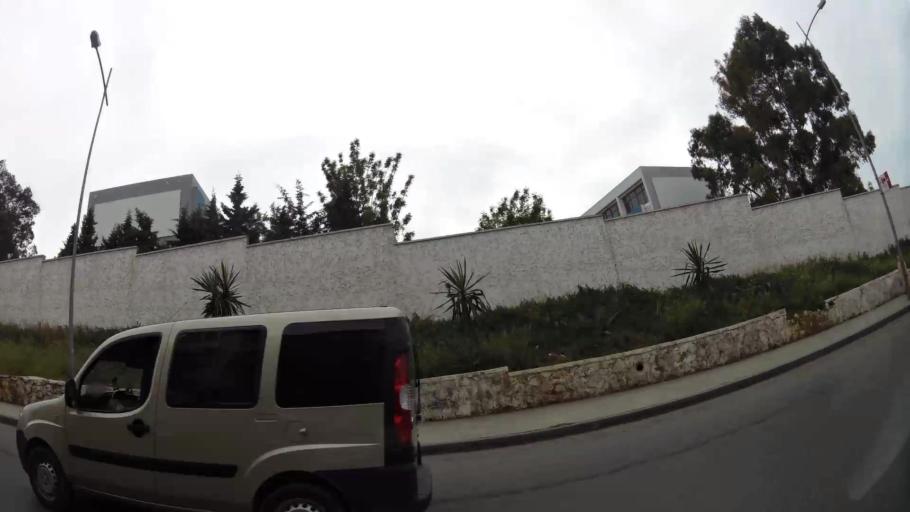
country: MA
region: Rabat-Sale-Zemmour-Zaer
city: Sale
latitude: 34.0342
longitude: -6.8060
